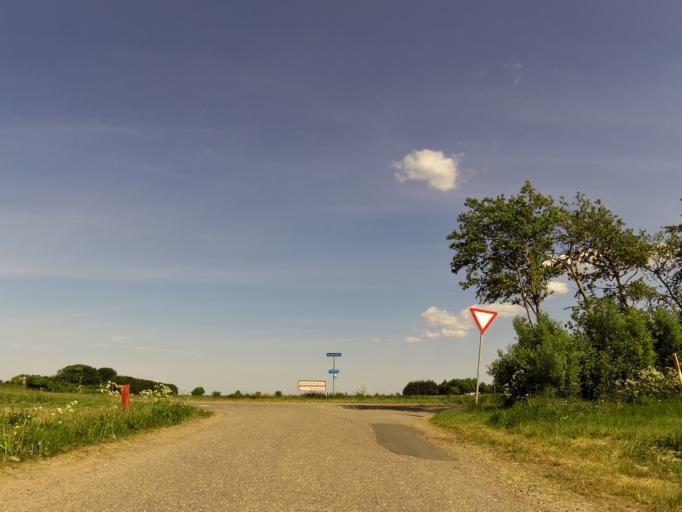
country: DK
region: Central Jutland
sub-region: Holstebro Kommune
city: Vinderup
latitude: 56.4355
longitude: 8.8703
